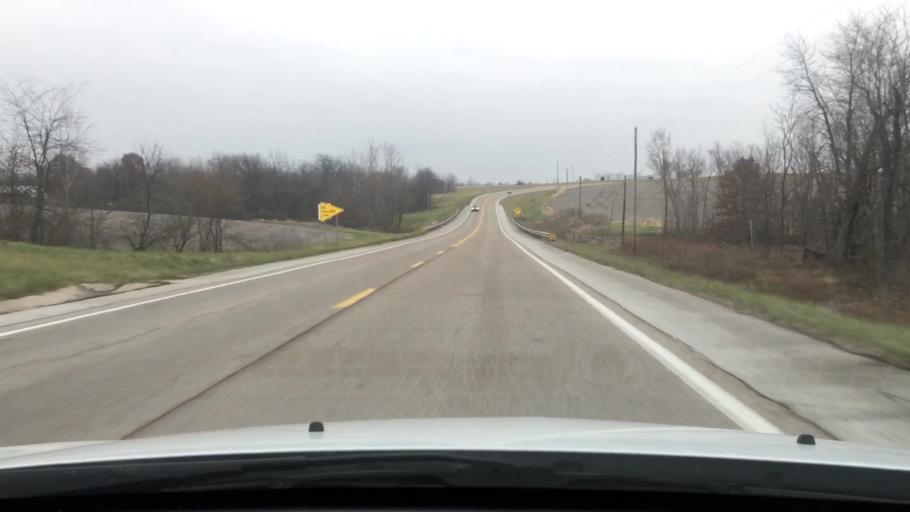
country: US
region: Illinois
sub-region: Pike County
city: Pittsfield
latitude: 39.6015
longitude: -90.8788
